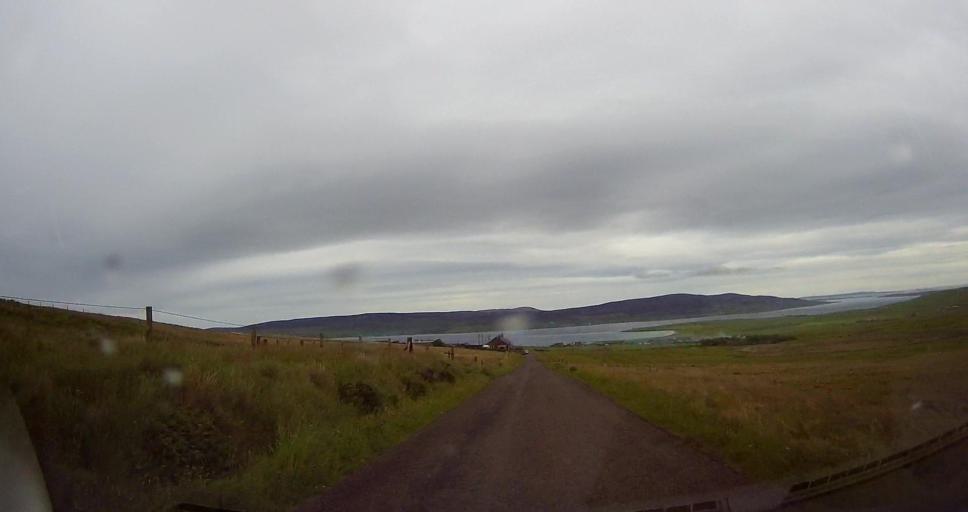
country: GB
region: Scotland
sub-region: Orkney Islands
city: Orkney
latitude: 59.1057
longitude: -3.1274
